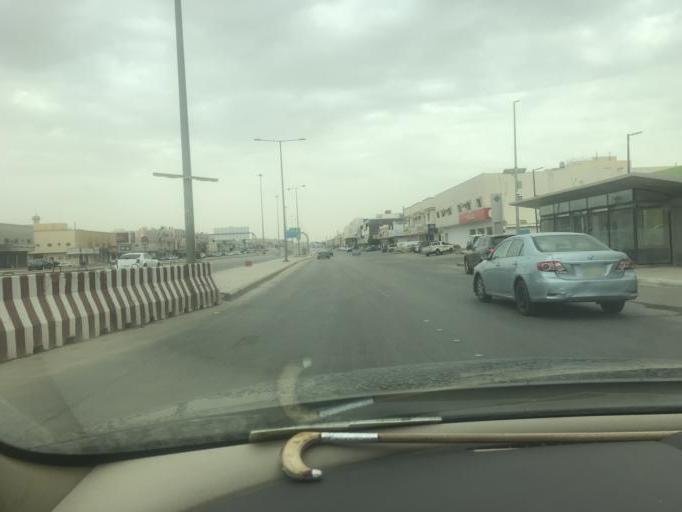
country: SA
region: Ar Riyad
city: Riyadh
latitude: 24.7989
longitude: 46.6972
